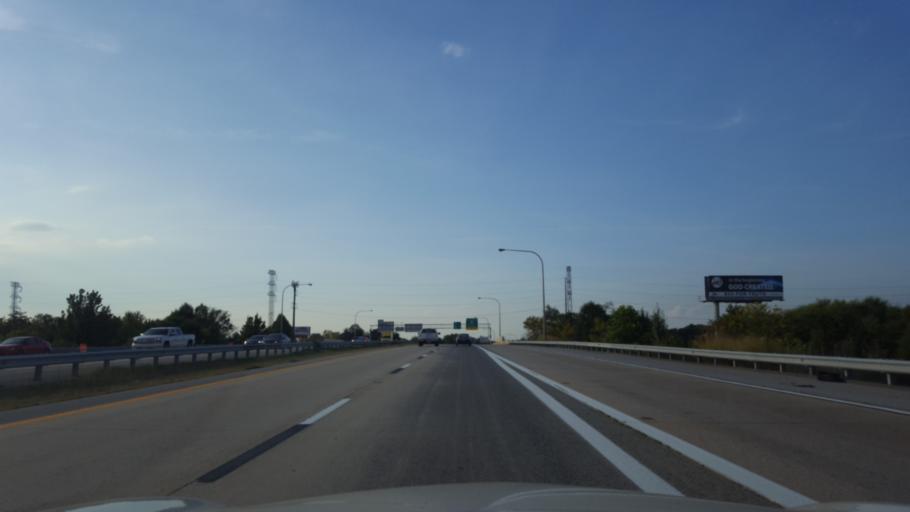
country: US
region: Delaware
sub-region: New Castle County
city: Newport
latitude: 39.7290
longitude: -75.6192
